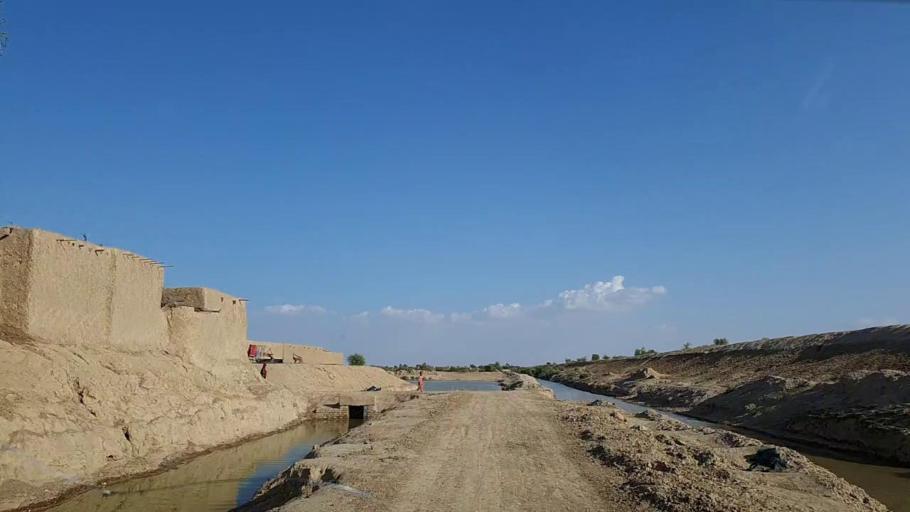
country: PK
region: Sindh
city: Johi
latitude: 26.5840
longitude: 67.5423
